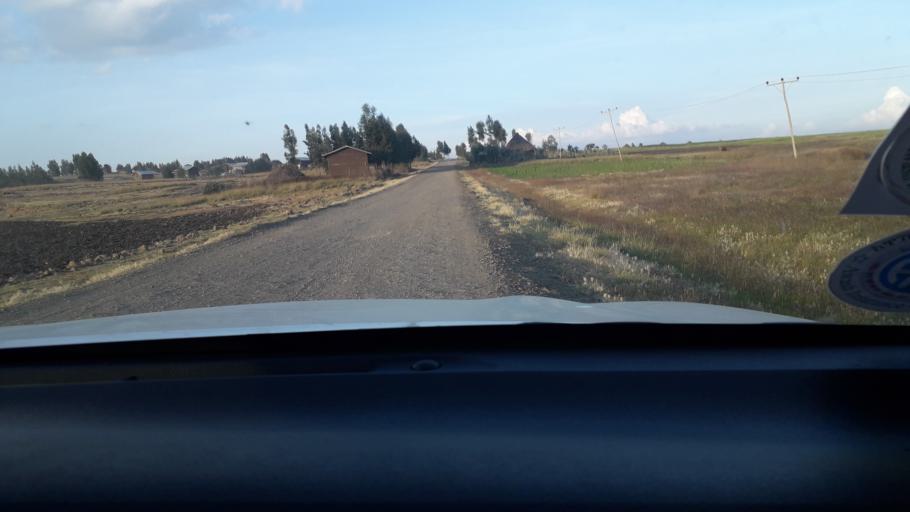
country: ET
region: Amhara
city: Lalibela
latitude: 11.5547
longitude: 39.2237
